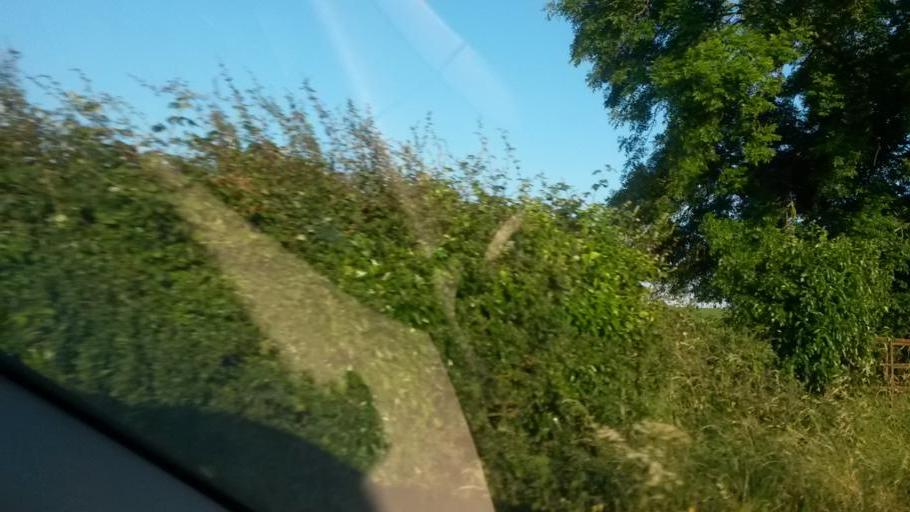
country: IE
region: Leinster
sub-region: An Mhi
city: Ashbourne
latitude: 53.5555
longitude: -6.3590
